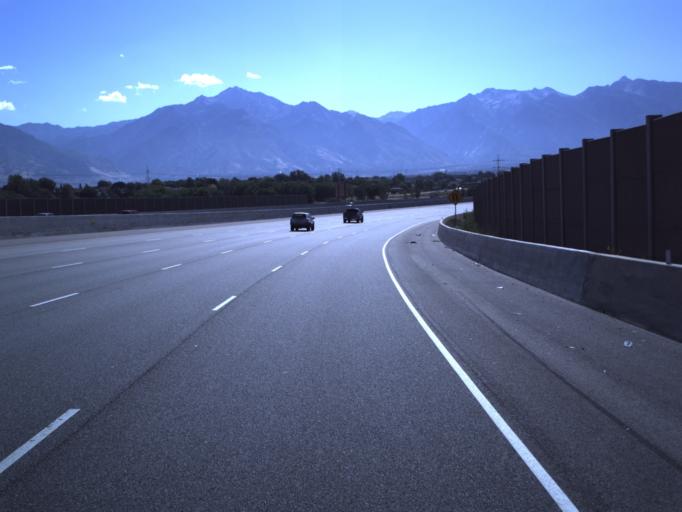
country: US
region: Utah
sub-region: Salt Lake County
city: Taylorsville
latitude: 40.6440
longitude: -111.9294
